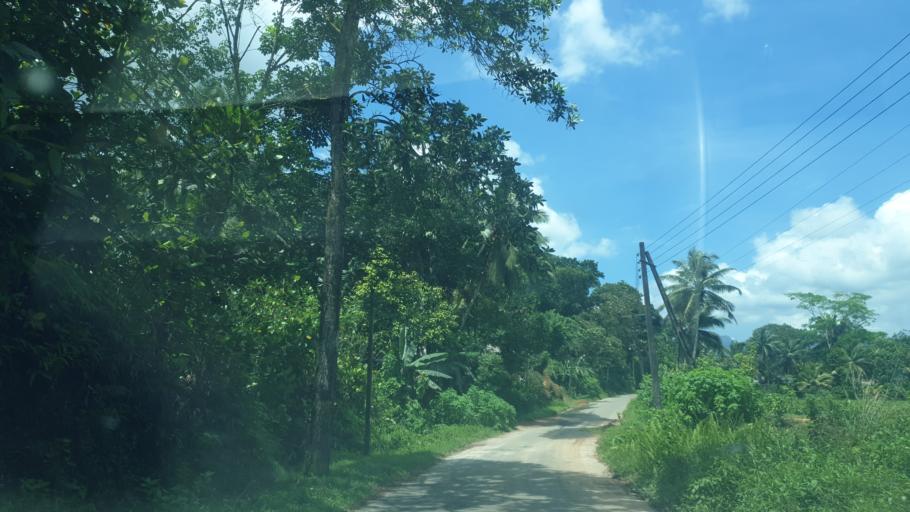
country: LK
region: Sabaragamuwa
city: Ratnapura
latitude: 6.4718
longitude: 80.4226
